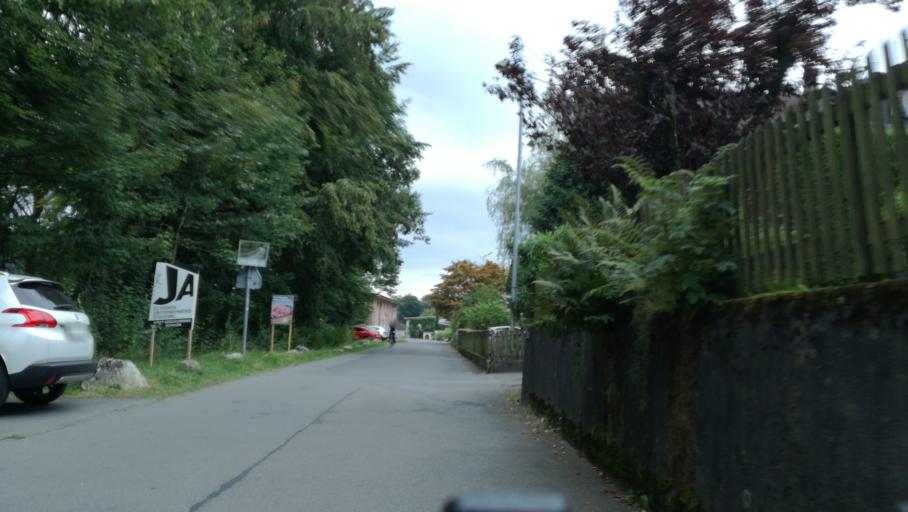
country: CH
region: Lucerne
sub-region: Lucerne-Land District
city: Ebikon
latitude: 47.0725
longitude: 8.3239
